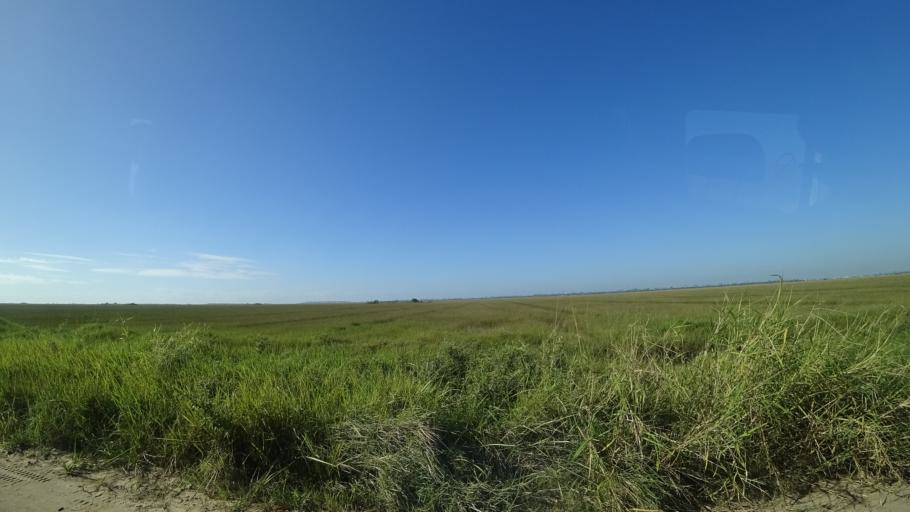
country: MZ
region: Sofala
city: Beira
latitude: -19.7572
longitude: 34.9209
